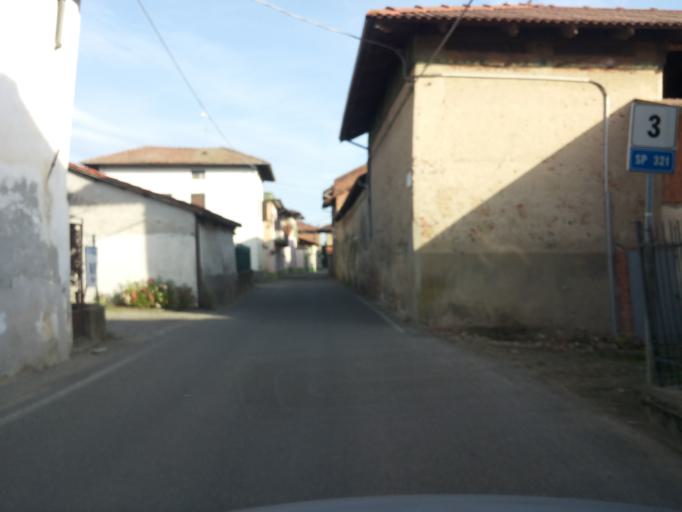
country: IT
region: Piedmont
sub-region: Provincia di Biella
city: Salussola
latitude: 45.4456
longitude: 8.1524
